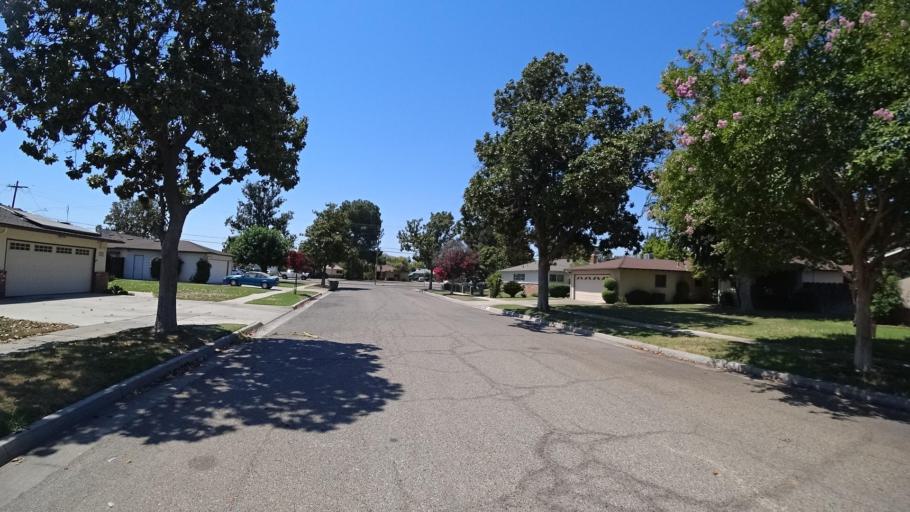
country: US
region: California
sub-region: Fresno County
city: Fresno
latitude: 36.8020
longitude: -119.7641
